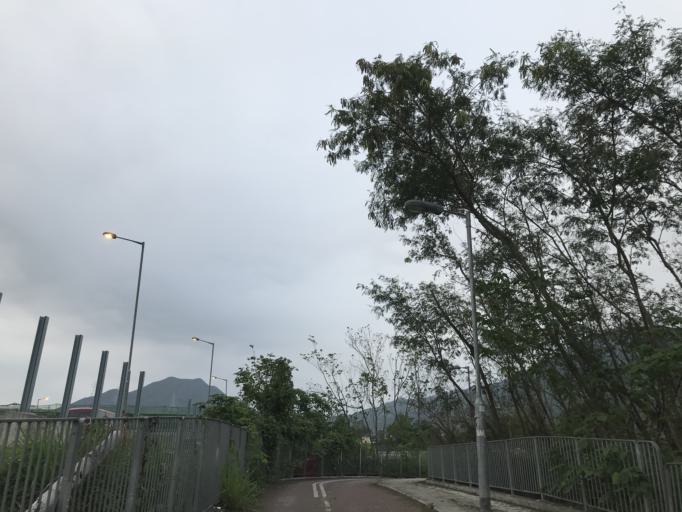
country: HK
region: Tai Po
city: Tai Po
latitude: 22.4669
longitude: 114.1522
